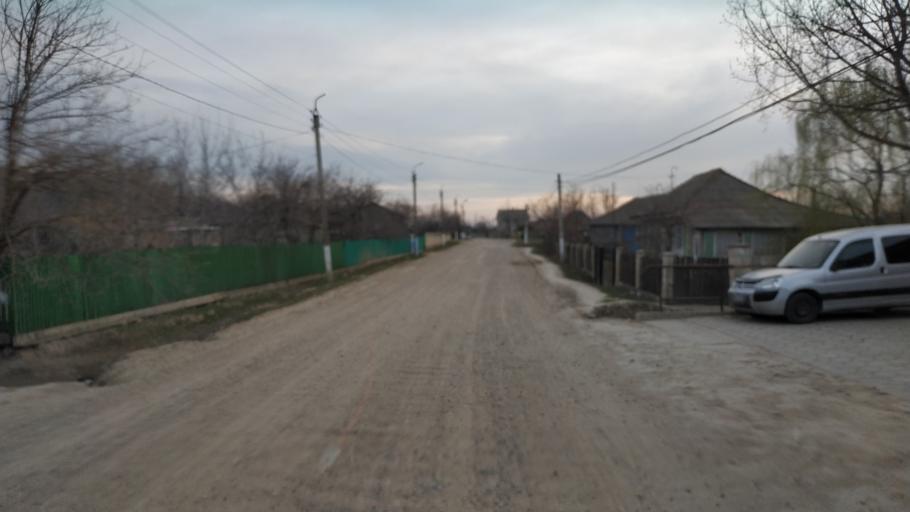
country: MD
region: Hincesti
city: Dancu
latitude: 46.7541
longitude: 28.2074
